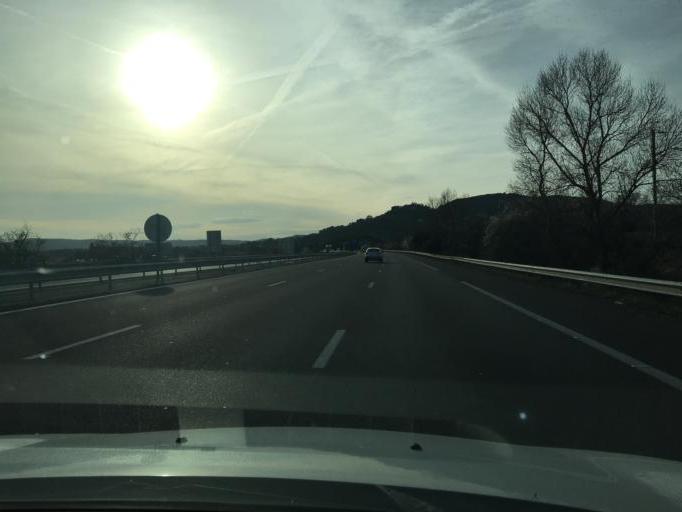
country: FR
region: Provence-Alpes-Cote d'Azur
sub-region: Departement du Var
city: Le Cannet-des-Maures
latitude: 43.4017
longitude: 6.3717
